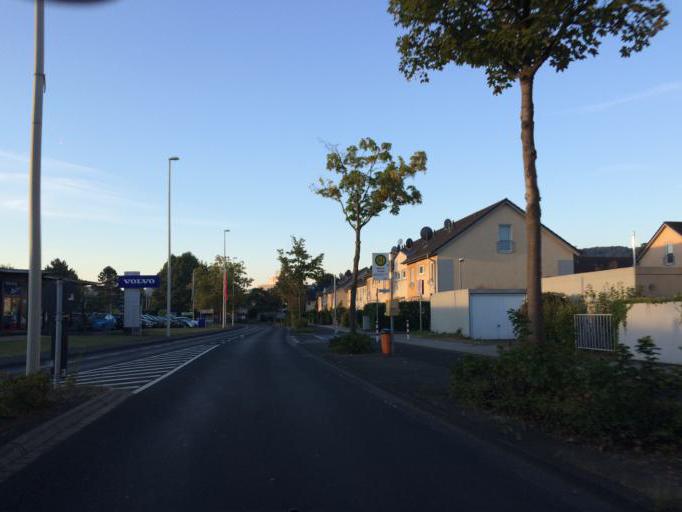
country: DE
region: North Rhine-Westphalia
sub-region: Regierungsbezirk Koln
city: Konigswinter
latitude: 50.6733
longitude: 7.1734
